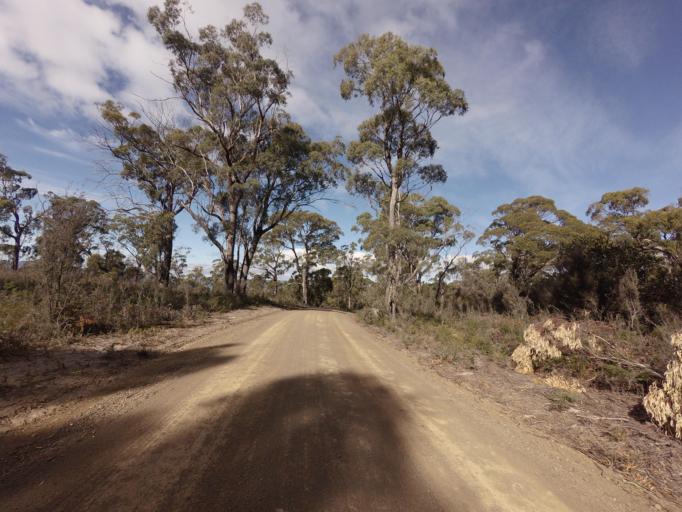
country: AU
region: Tasmania
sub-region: Clarence
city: Sandford
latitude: -42.9710
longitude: 147.7162
